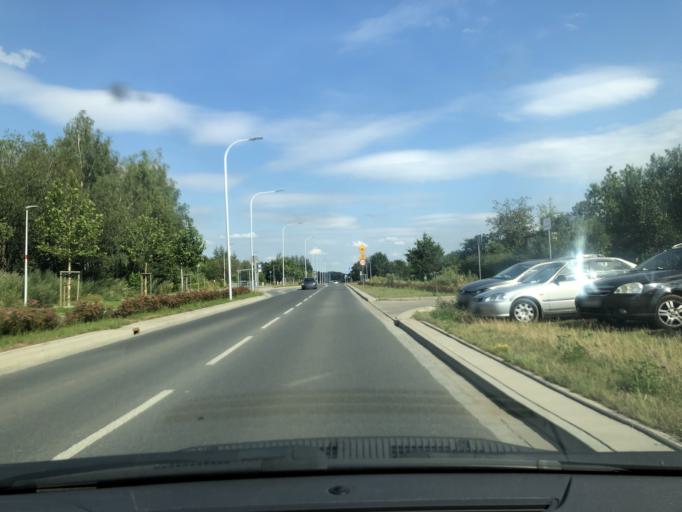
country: PL
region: Lower Silesian Voivodeship
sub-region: Powiat wroclawski
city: Smolec
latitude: 51.1533
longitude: 16.9030
